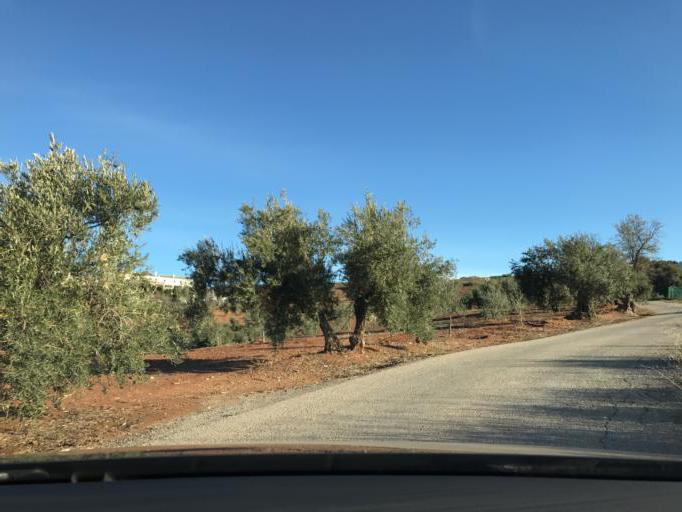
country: ES
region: Andalusia
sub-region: Provincia de Granada
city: Calicasas
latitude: 37.2757
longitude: -3.6225
